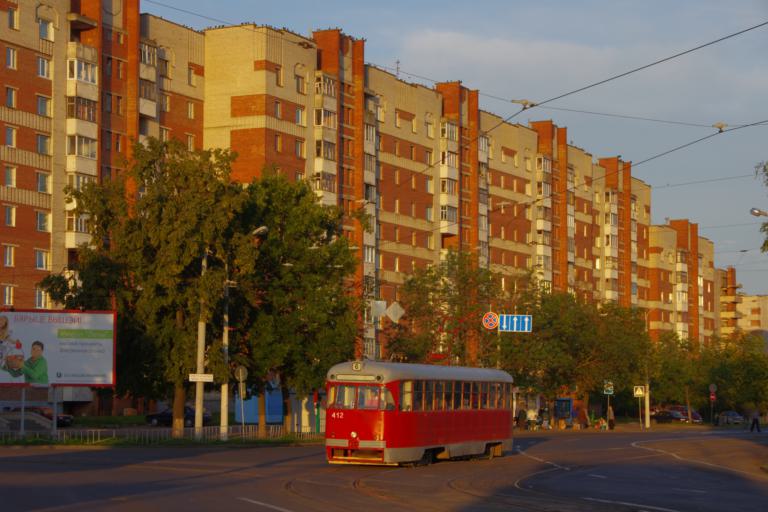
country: BY
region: Vitebsk
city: Vitebsk
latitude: 55.1992
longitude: 30.1835
